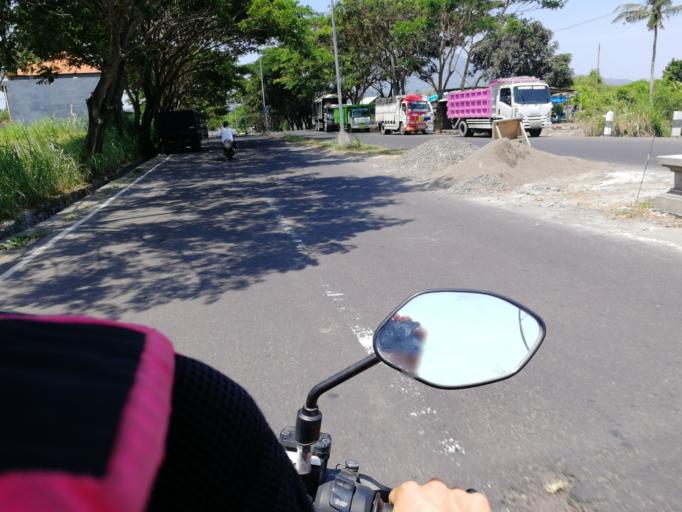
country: ID
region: Bali
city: Banjar Beji
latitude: -8.4458
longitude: 115.5886
